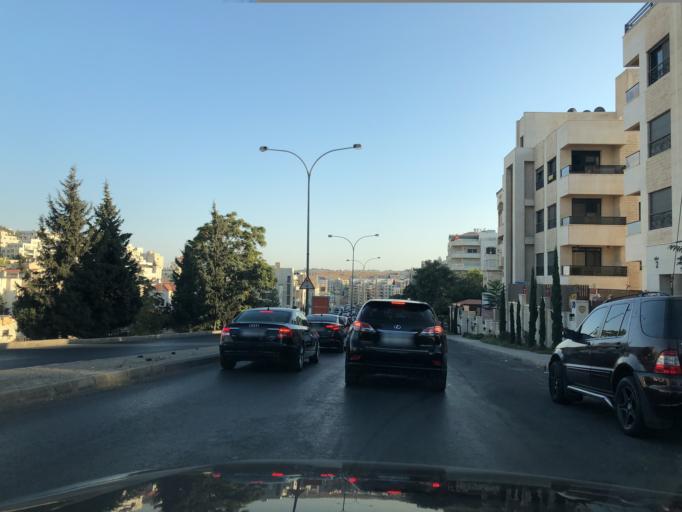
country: JO
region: Amman
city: Wadi as Sir
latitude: 31.9440
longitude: 35.8700
